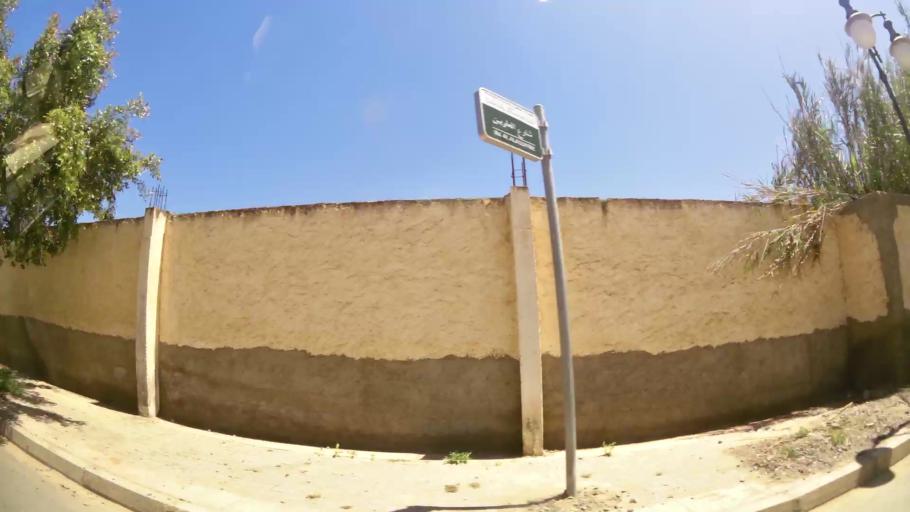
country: MA
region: Oriental
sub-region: Berkane-Taourirt
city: Madagh
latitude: 35.0752
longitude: -2.2215
